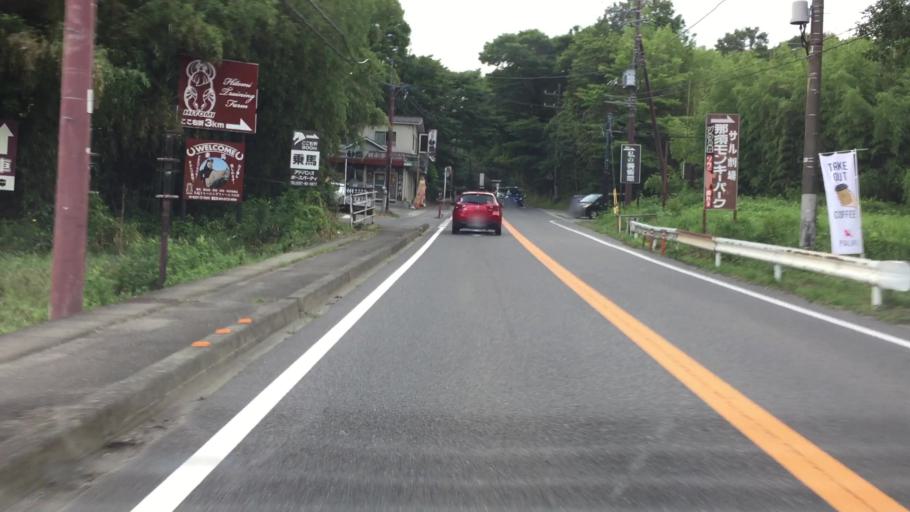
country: JP
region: Tochigi
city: Kuroiso
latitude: 37.0107
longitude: 140.0310
